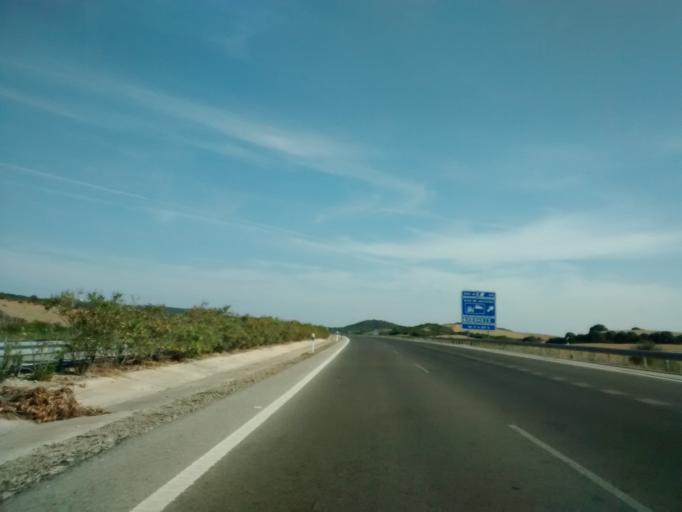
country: ES
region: Andalusia
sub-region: Provincia de Cadiz
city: Conil de la Frontera
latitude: 36.3001
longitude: -6.0563
